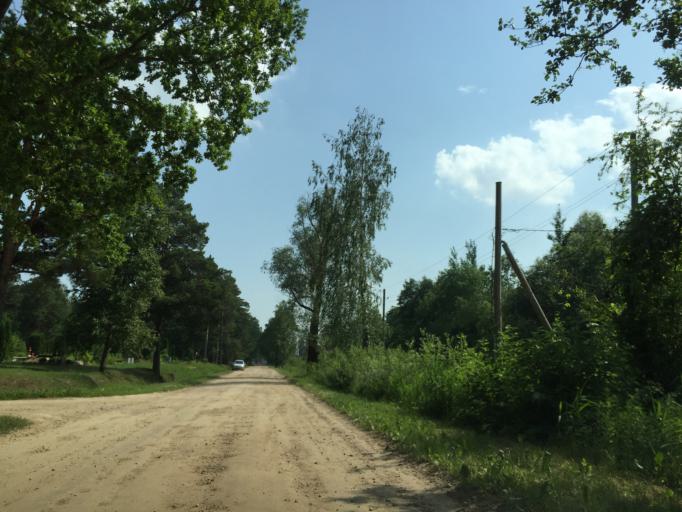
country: LV
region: Jelgava
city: Jelgava
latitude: 56.6755
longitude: 23.7408
